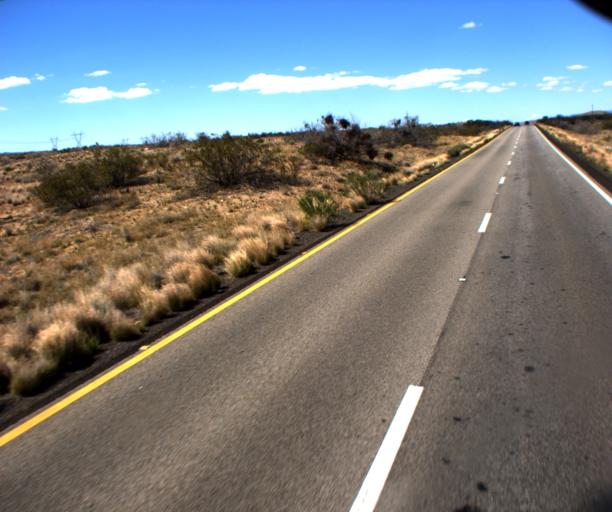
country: US
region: Arizona
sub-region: Mohave County
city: Kingman
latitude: 34.9744
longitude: -113.6689
